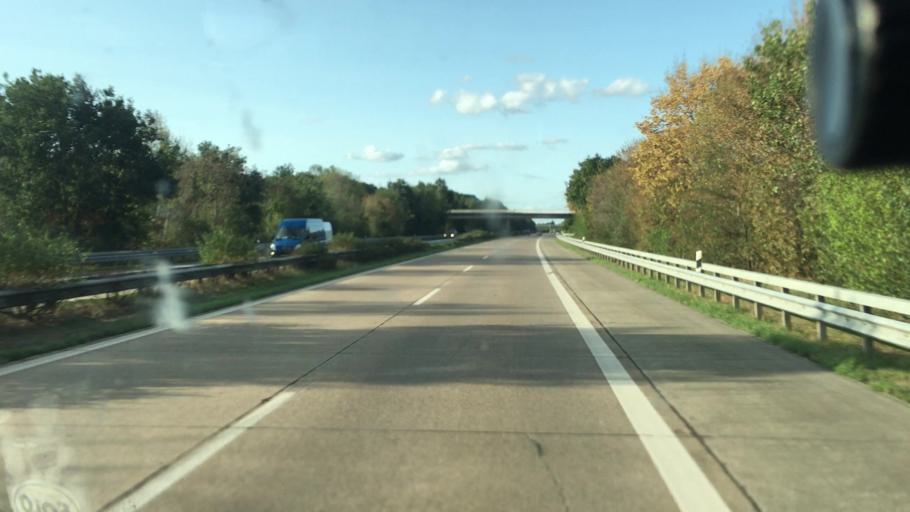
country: DE
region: Lower Saxony
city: Wiefelstede
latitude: 53.2960
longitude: 8.1470
